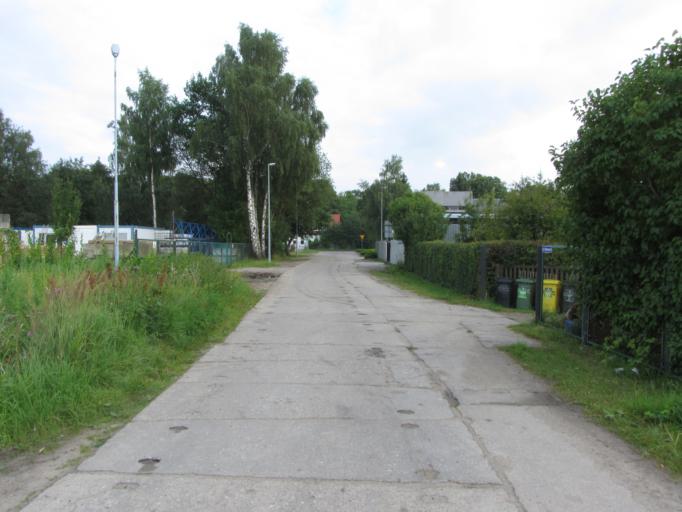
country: PL
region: West Pomeranian Voivodeship
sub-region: Powiat kolobrzeski
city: Kolobrzeg
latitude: 54.1592
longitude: 15.5625
